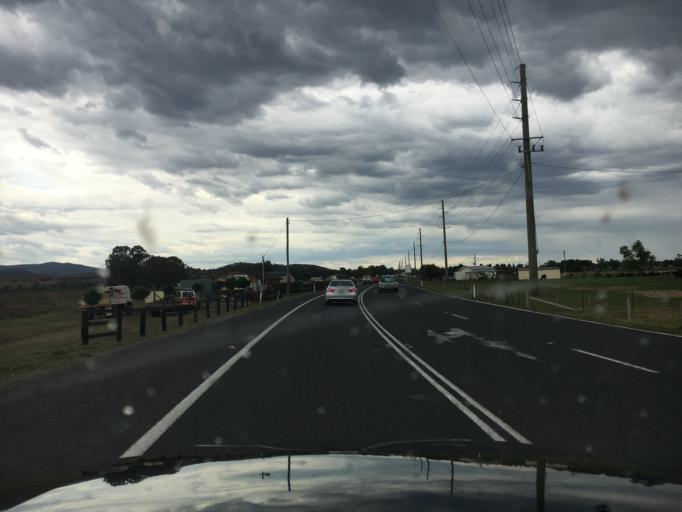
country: AU
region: New South Wales
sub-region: Muswellbrook
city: Muswellbrook
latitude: -32.1452
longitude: 150.8828
